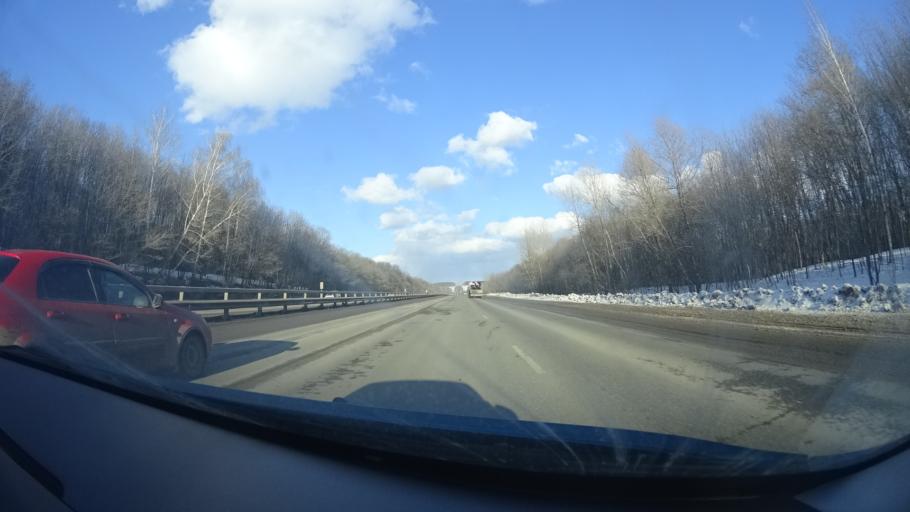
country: RU
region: Bashkortostan
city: Avdon
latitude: 54.6448
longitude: 55.6295
